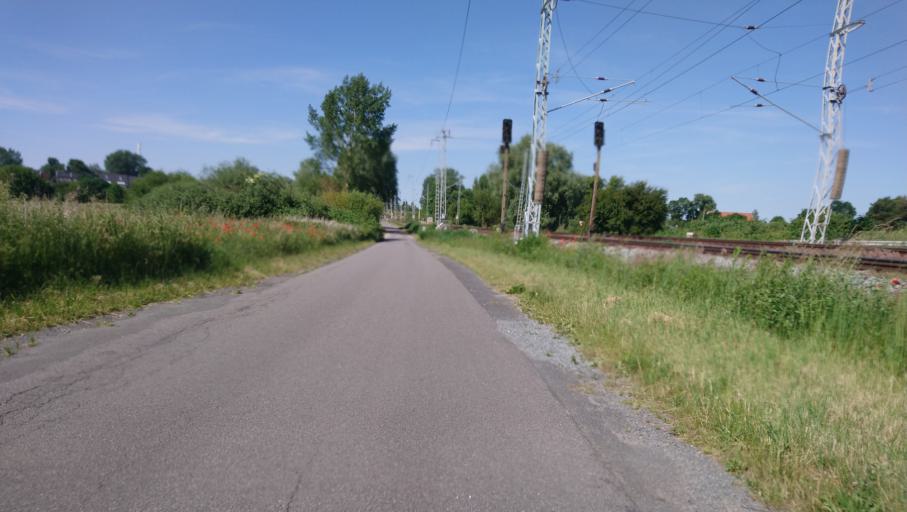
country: DE
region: Mecklenburg-Vorpommern
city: Dierkow-Neu
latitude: 54.0905
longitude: 12.1794
